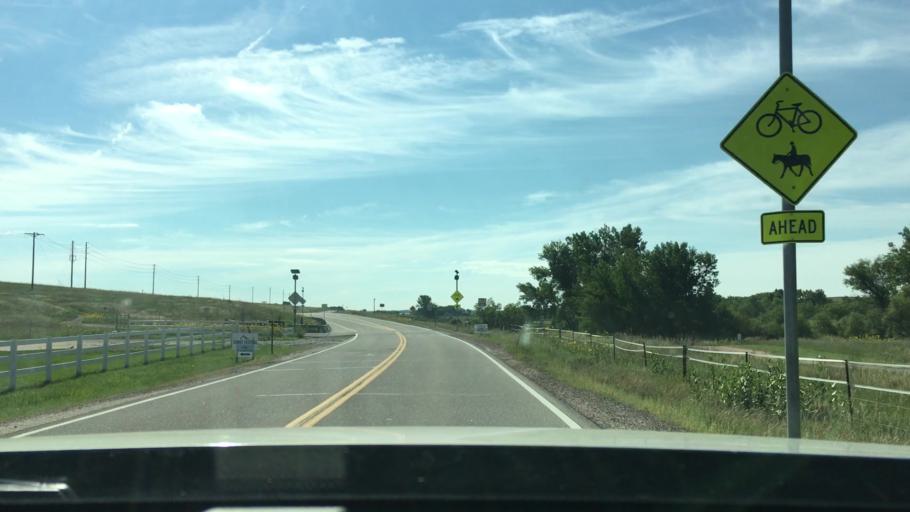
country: US
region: Colorado
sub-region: Douglas County
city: The Pinery
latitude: 39.4295
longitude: -104.7430
